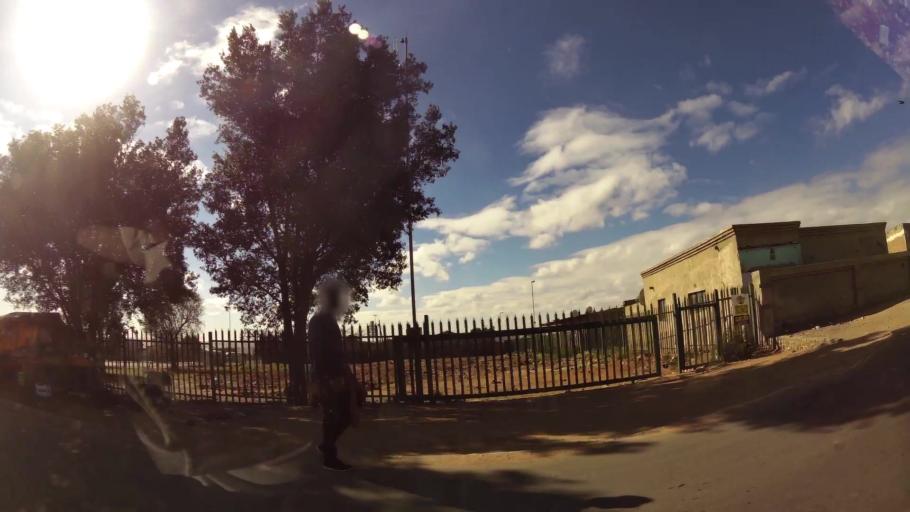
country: ZA
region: Gauteng
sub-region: City of Johannesburg Metropolitan Municipality
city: Modderfontein
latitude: -26.0449
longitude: 28.1781
